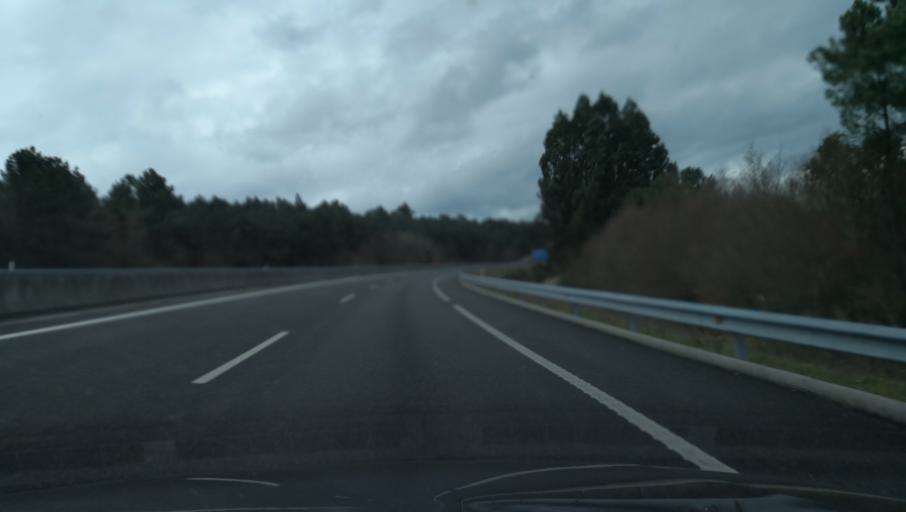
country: ES
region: Galicia
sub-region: Provincia de Ourense
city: Maside
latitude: 42.4354
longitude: -8.0182
